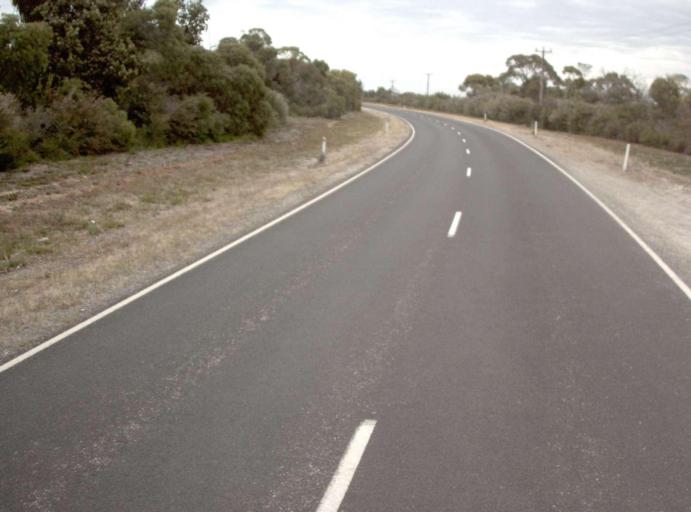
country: AU
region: Victoria
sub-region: Wellington
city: Sale
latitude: -38.1837
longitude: 147.3733
